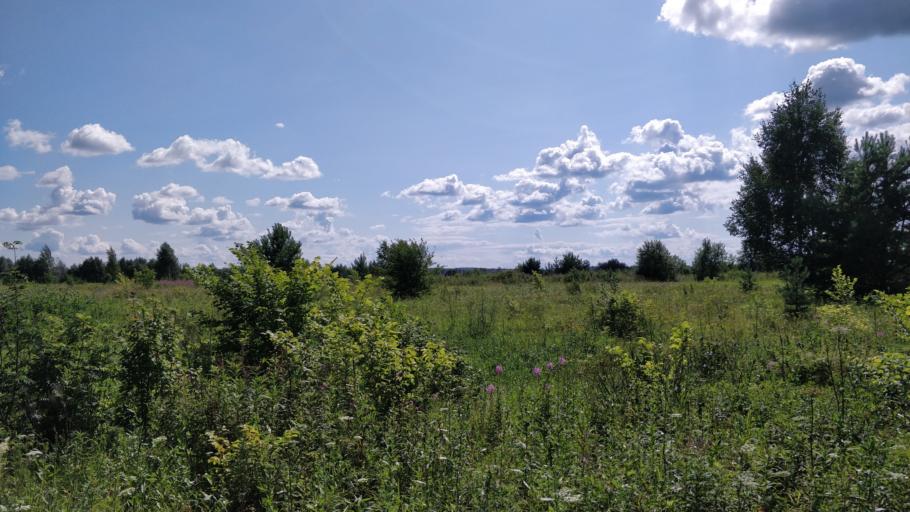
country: RU
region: Perm
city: Ust'-Kachka
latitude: 57.9939
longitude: 55.6866
